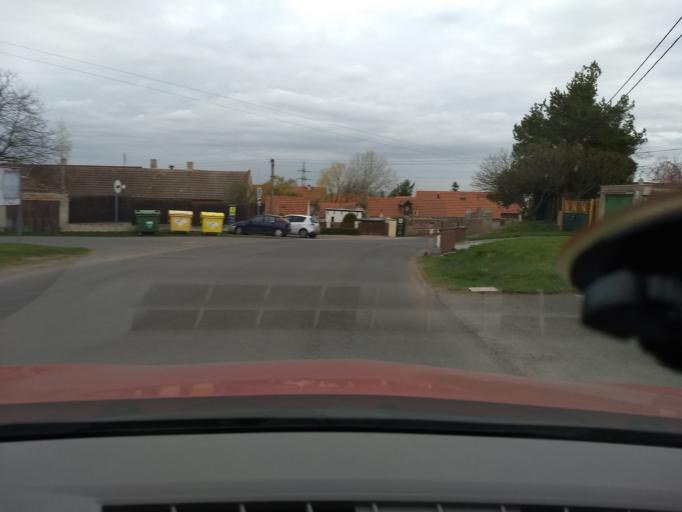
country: CZ
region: Central Bohemia
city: Unhost'
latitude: 50.0645
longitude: 14.1649
